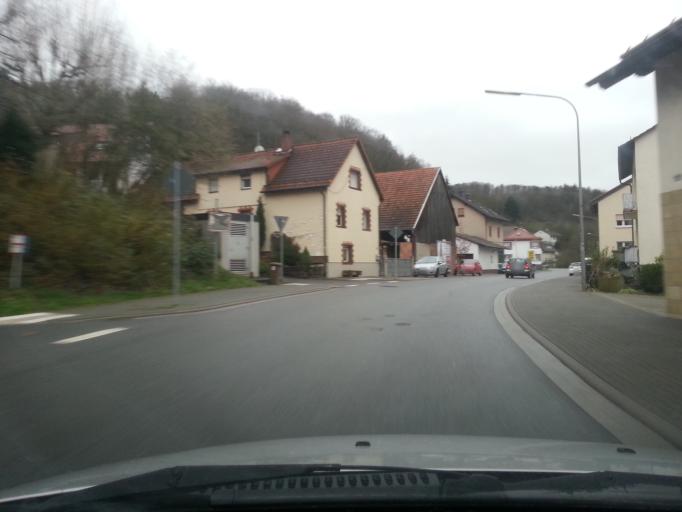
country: DE
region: Hesse
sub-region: Regierungsbezirk Darmstadt
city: Morlenbach
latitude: 49.5844
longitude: 8.7696
